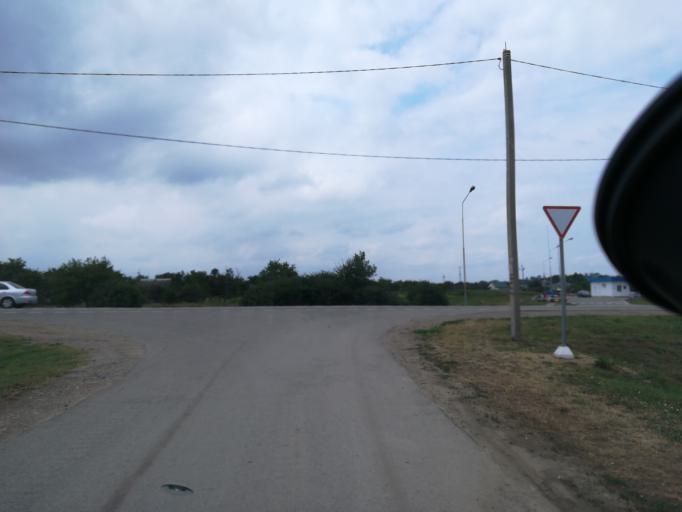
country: RU
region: Krasnodarskiy
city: Korzhevskiy
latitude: 45.1956
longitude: 37.6736
